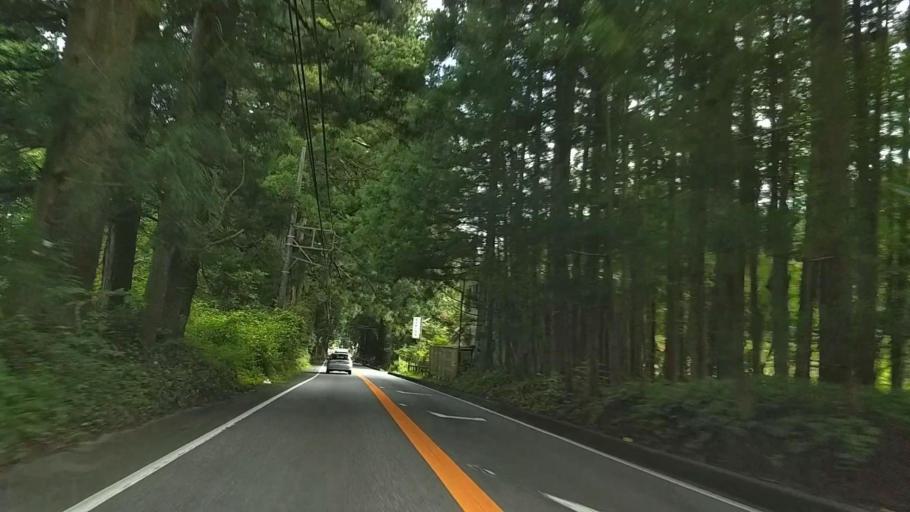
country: JP
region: Tochigi
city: Nikko
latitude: 36.7389
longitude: 139.6377
